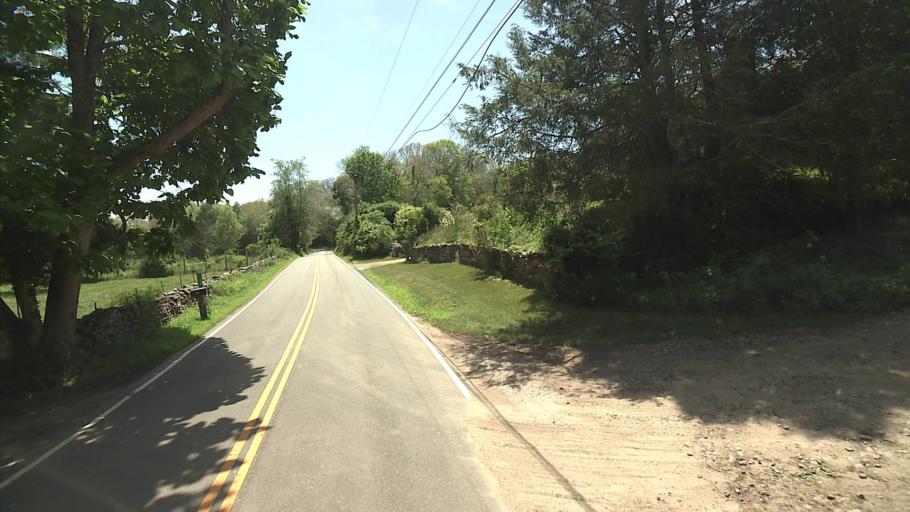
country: US
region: Connecticut
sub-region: Middlesex County
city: Essex Village
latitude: 41.4508
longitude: -72.3390
